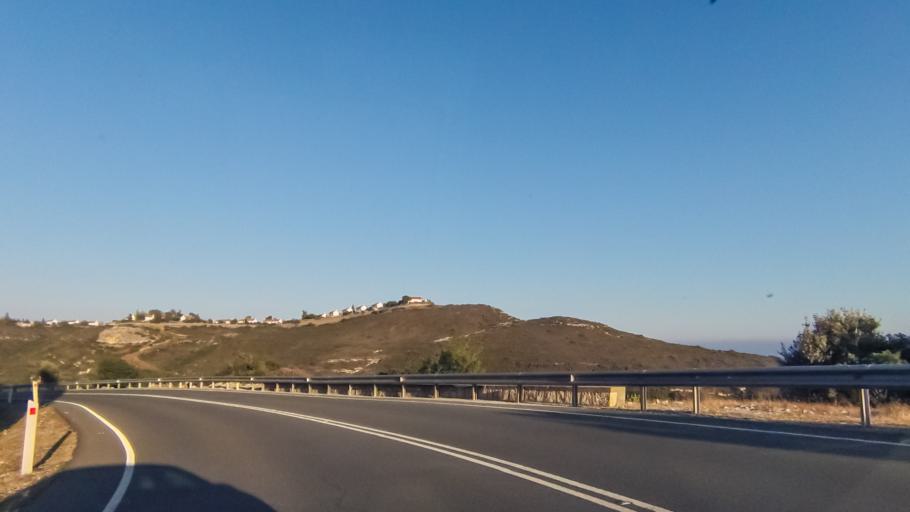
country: CY
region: Limassol
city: Sotira
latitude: 34.6724
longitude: 32.8170
